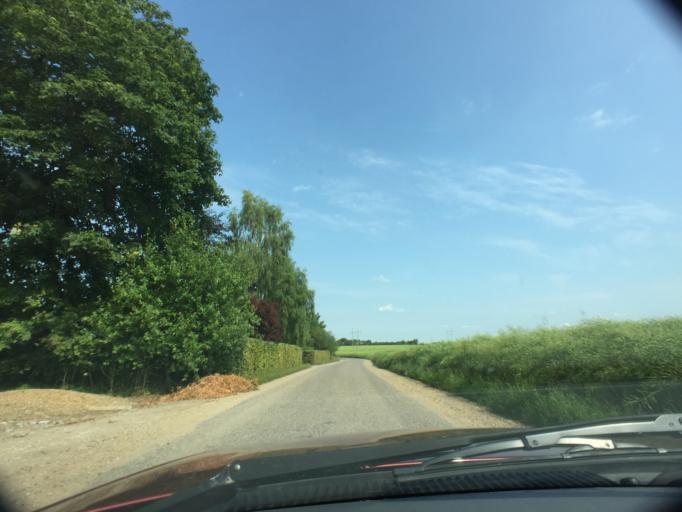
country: DK
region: Central Jutland
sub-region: Favrskov Kommune
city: Hammel
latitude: 56.2449
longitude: 9.7487
